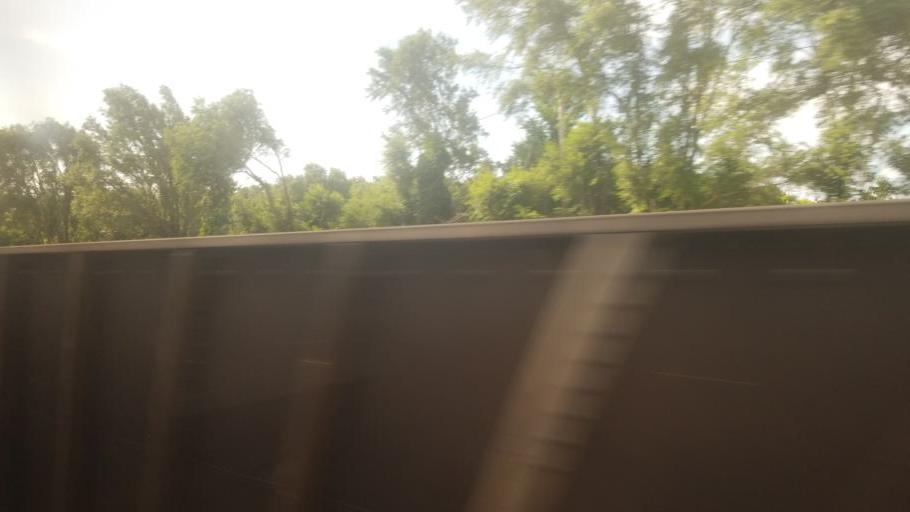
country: US
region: Kansas
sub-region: Johnson County
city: De Soto
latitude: 38.9808
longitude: -94.9538
